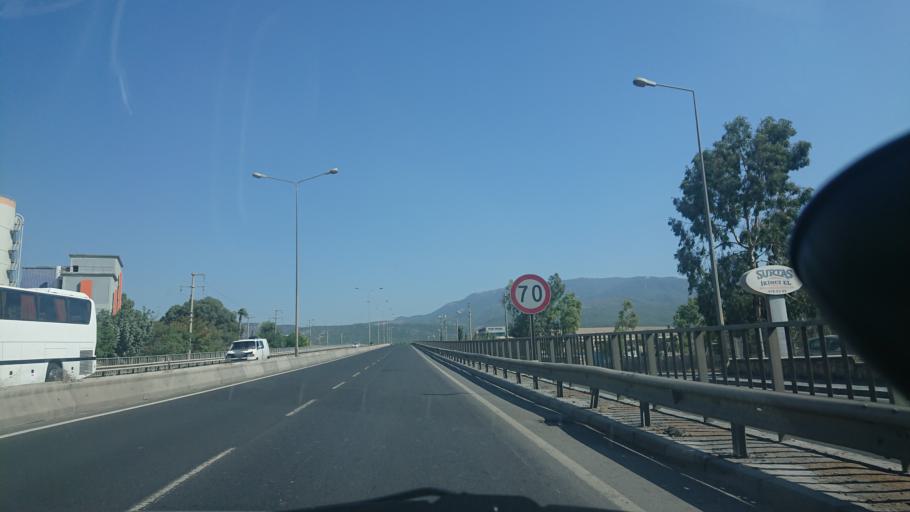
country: TR
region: Izmir
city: Bornova
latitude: 38.4537
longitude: 27.2622
